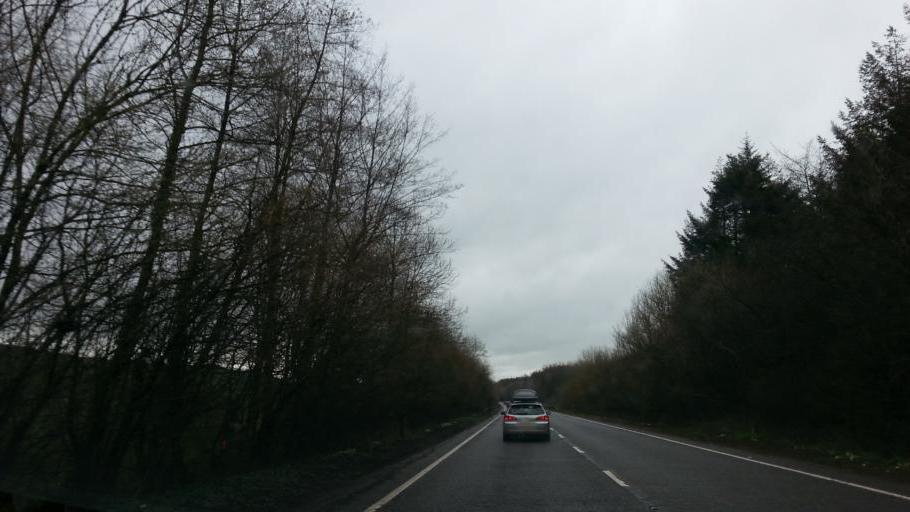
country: GB
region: England
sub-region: Devon
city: South Molton
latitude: 51.0509
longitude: -3.9384
